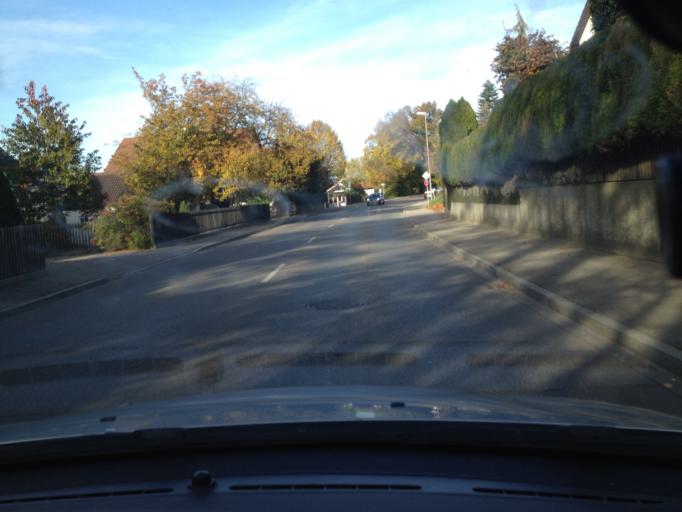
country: DE
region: Bavaria
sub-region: Swabia
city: Wehringen
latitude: 48.2487
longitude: 10.8027
